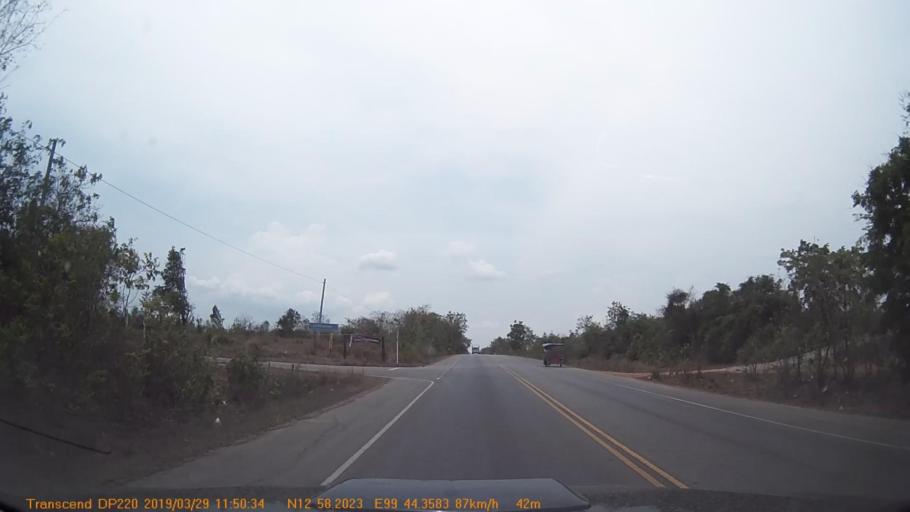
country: TH
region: Phetchaburi
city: Kaeng Krachan
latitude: 12.9698
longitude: 99.7394
